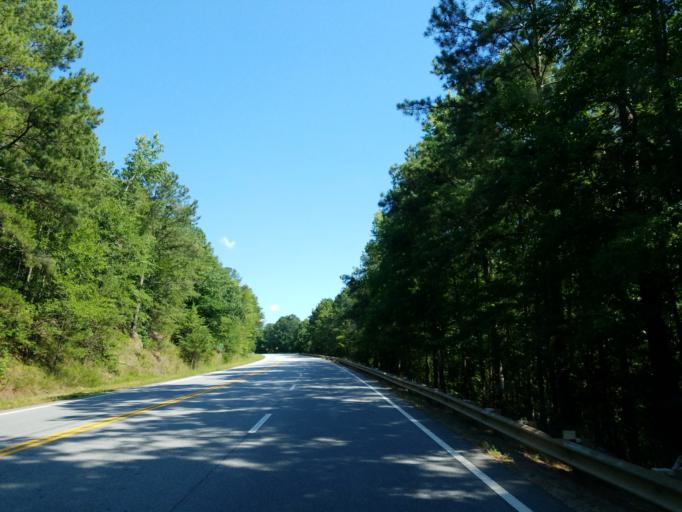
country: US
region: Georgia
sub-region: Crawford County
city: Roberta
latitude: 32.8259
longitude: -84.0600
